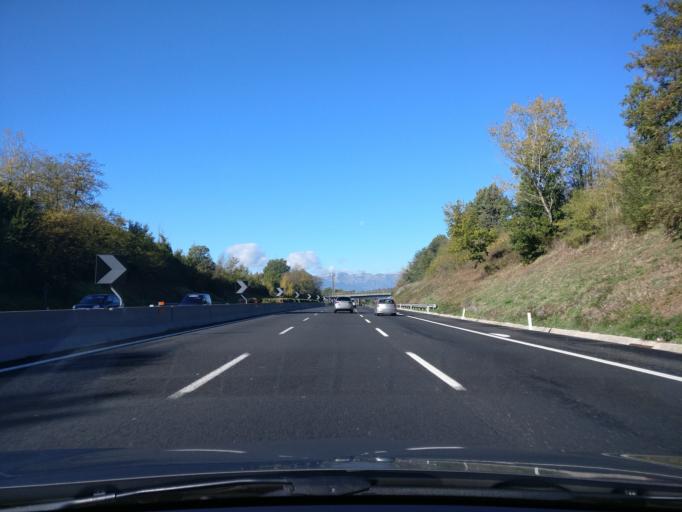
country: IT
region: Latium
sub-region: Provincia di Frosinone
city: Pofi
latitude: 41.5575
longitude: 13.4160
